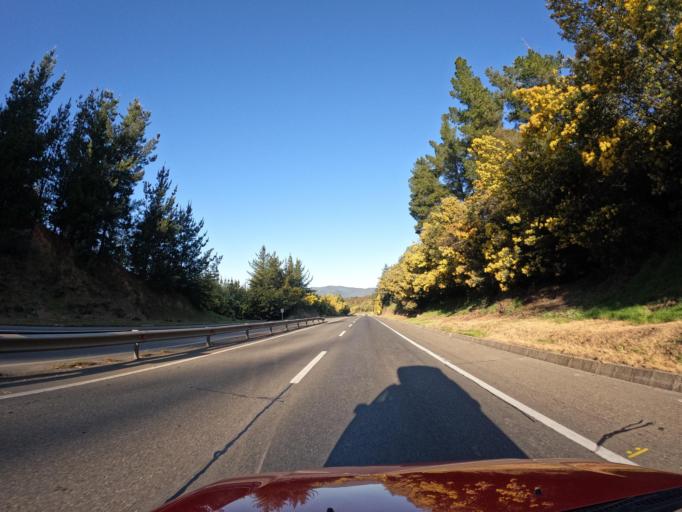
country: CL
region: Biobio
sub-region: Provincia de Concepcion
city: Tome
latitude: -36.6976
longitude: -72.6312
